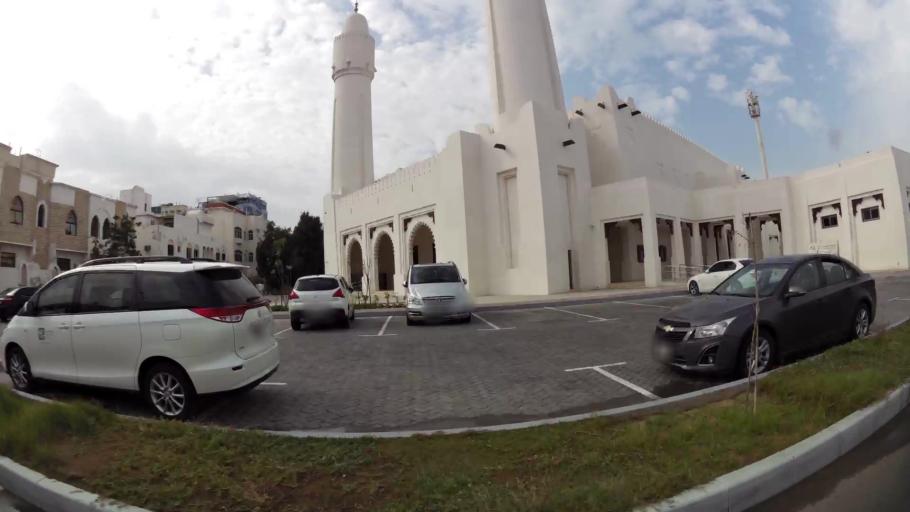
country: AE
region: Abu Dhabi
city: Abu Dhabi
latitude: 24.4417
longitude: 54.4103
